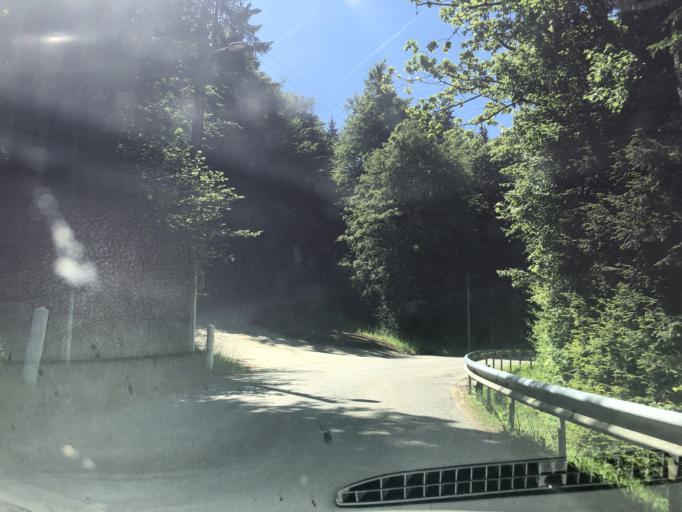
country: FR
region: Rhone-Alpes
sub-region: Departement de la Haute-Savoie
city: Menthon-Saint-Bernard
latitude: 45.8658
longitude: 6.2186
